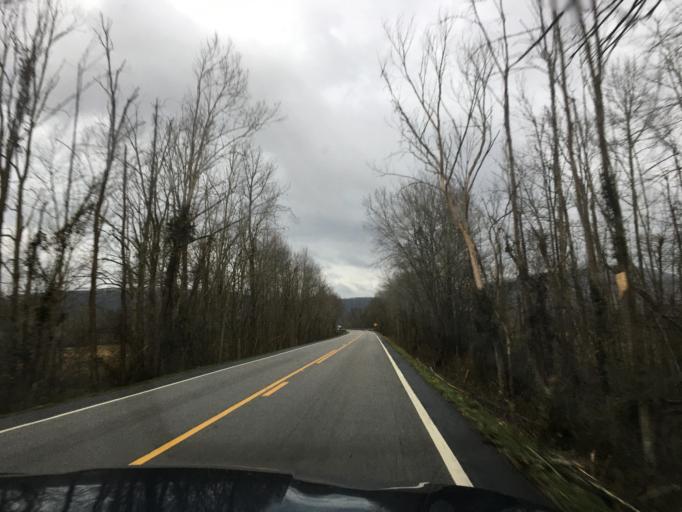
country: US
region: Tennessee
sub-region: Cumberland County
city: Lake Tansi
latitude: 35.8453
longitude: -84.9179
